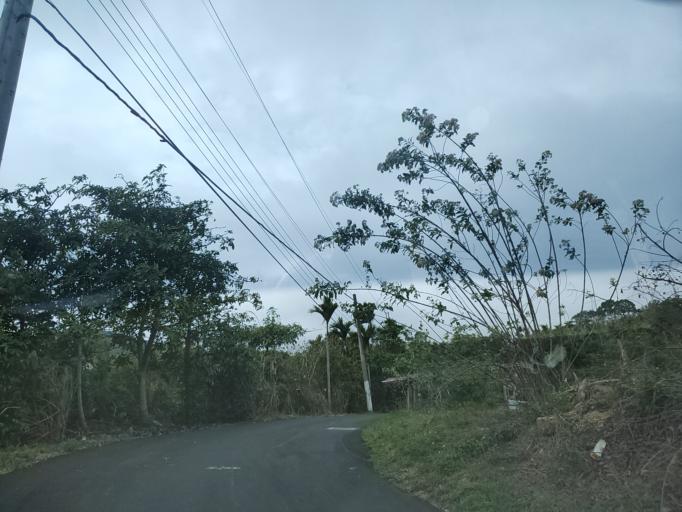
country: TW
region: Taiwan
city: Fengyuan
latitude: 24.3581
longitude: 120.7786
